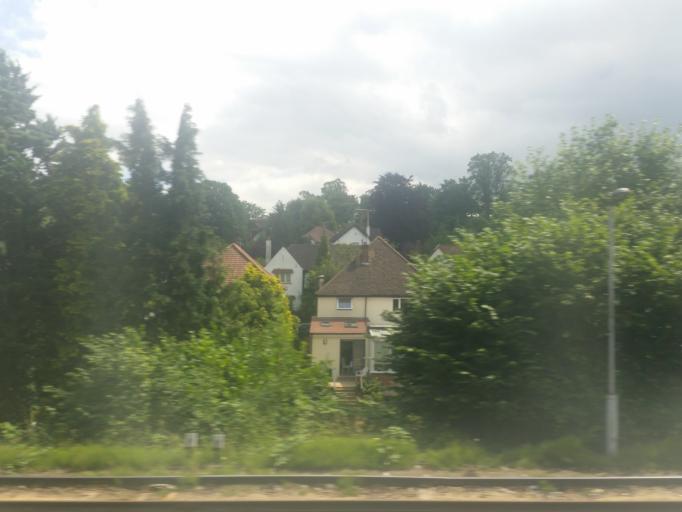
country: GB
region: England
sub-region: Greater London
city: Purley
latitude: 51.3401
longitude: -0.1096
